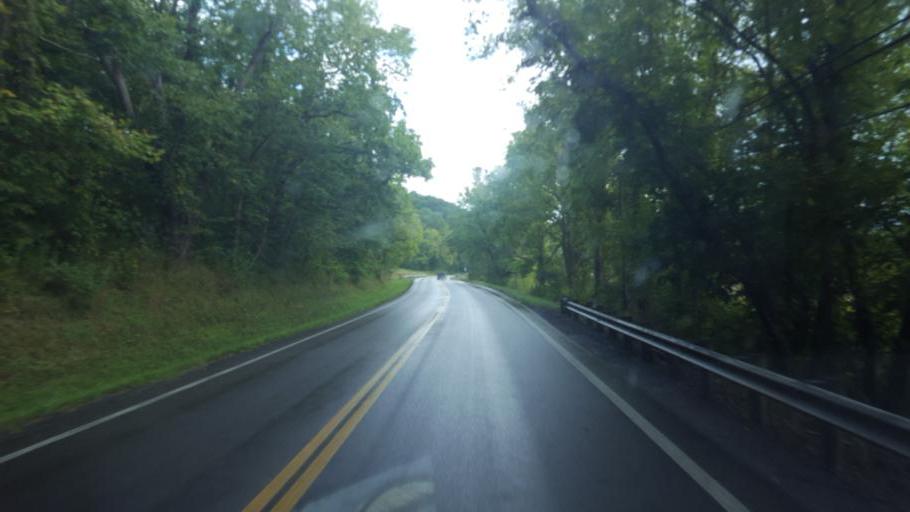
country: US
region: Ohio
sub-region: Holmes County
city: Millersburg
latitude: 40.5225
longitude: -81.9212
